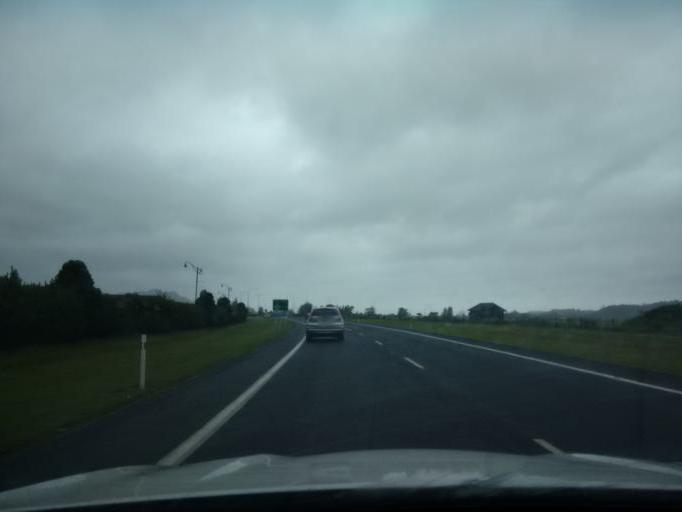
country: NZ
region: Waikato
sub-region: Thames-Coromandel District
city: Whitianga
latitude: -36.8317
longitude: 175.6821
